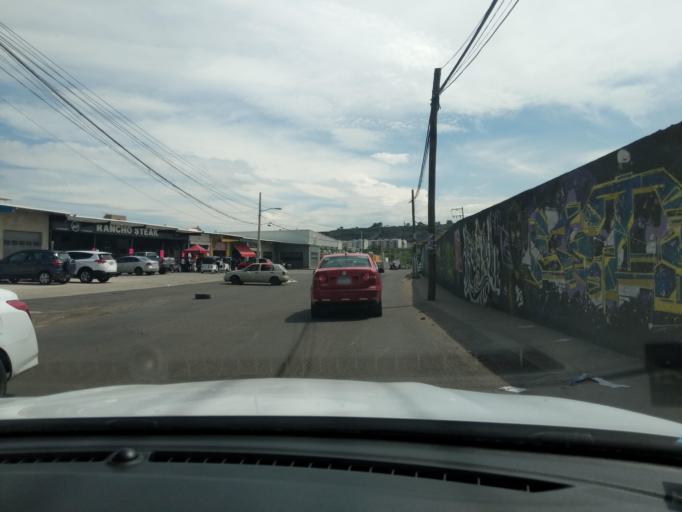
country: MX
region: Jalisco
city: Tonala
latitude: 20.6471
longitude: -103.2274
